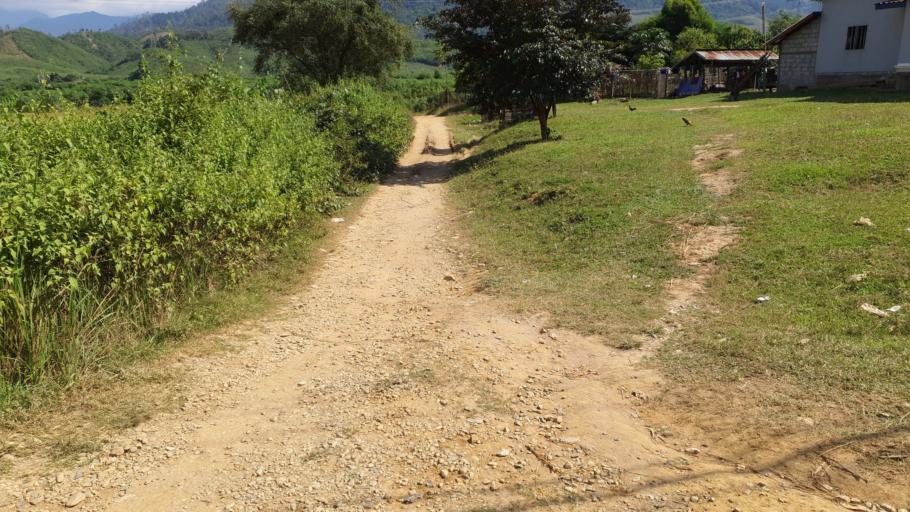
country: LA
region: Bolikhamxai
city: Bolikhan
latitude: 18.9054
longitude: 103.7401
